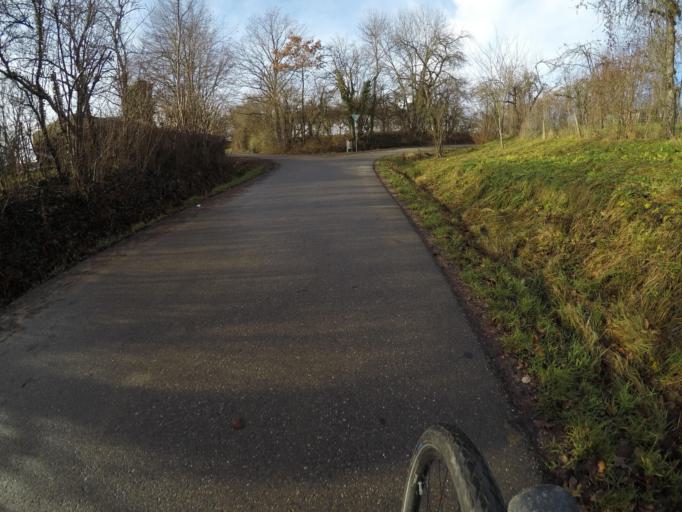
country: DE
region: Baden-Wuerttemberg
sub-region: Regierungsbezirk Stuttgart
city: Dettingen unter Teck
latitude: 48.6192
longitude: 9.4432
